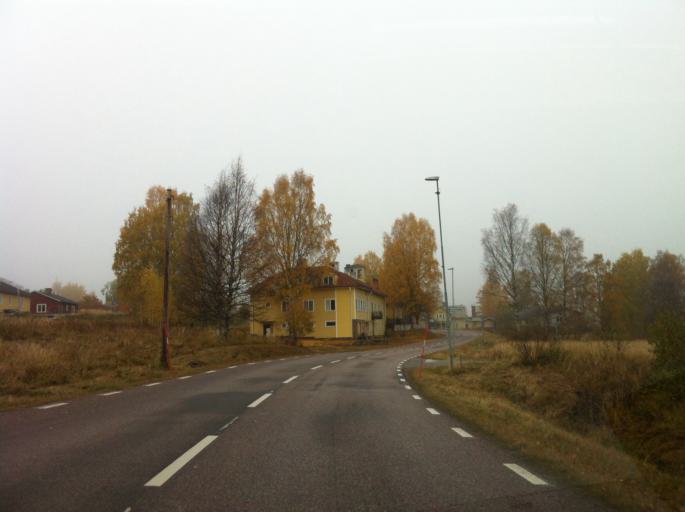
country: NO
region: Hedmark
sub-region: Trysil
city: Innbygda
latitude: 61.6909
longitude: 13.1509
